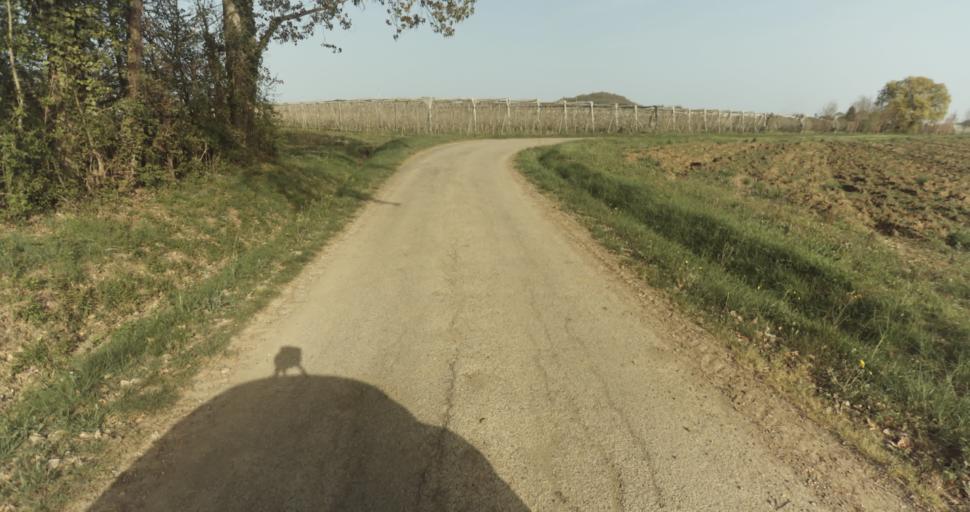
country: FR
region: Midi-Pyrenees
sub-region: Departement du Tarn-et-Garonne
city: Moissac
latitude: 44.1172
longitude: 1.1366
